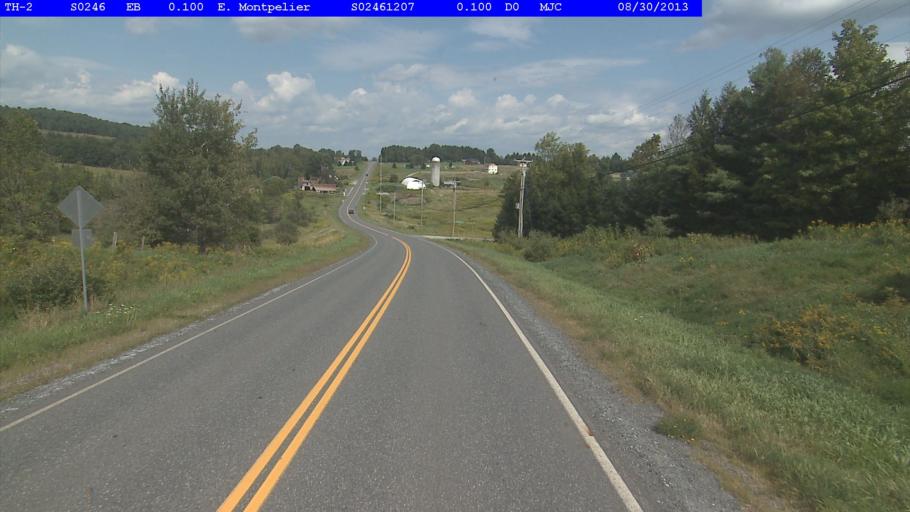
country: US
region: Vermont
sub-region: Washington County
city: Montpelier
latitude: 44.2543
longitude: -72.5199
